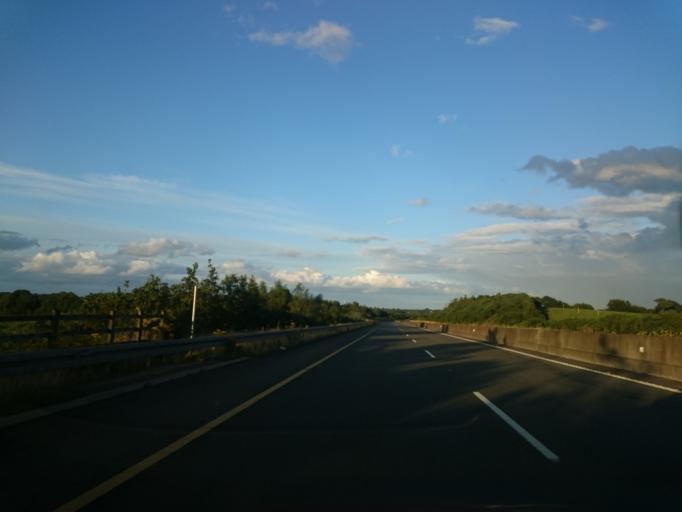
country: IE
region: Leinster
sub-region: Loch Garman
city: Gorey
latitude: 52.6344
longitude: -6.3575
